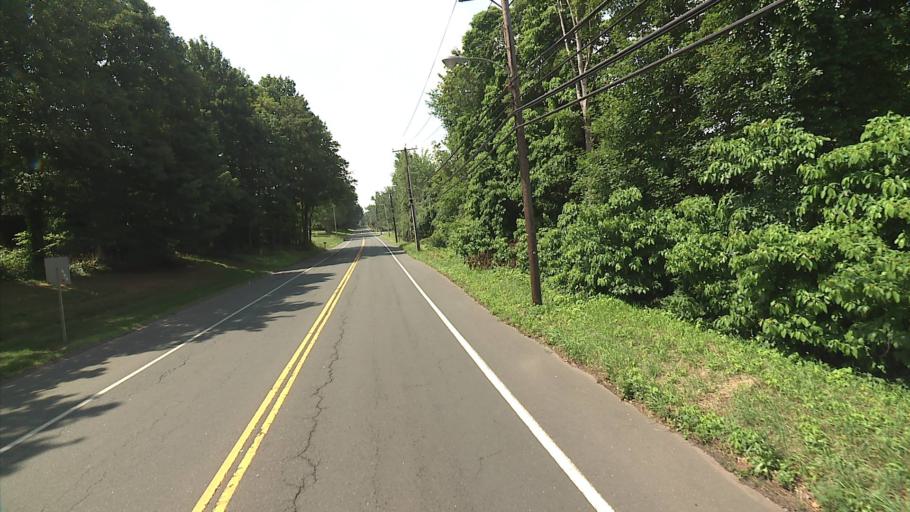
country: US
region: Connecticut
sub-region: Middlesex County
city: Cromwell
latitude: 41.5965
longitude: -72.6962
